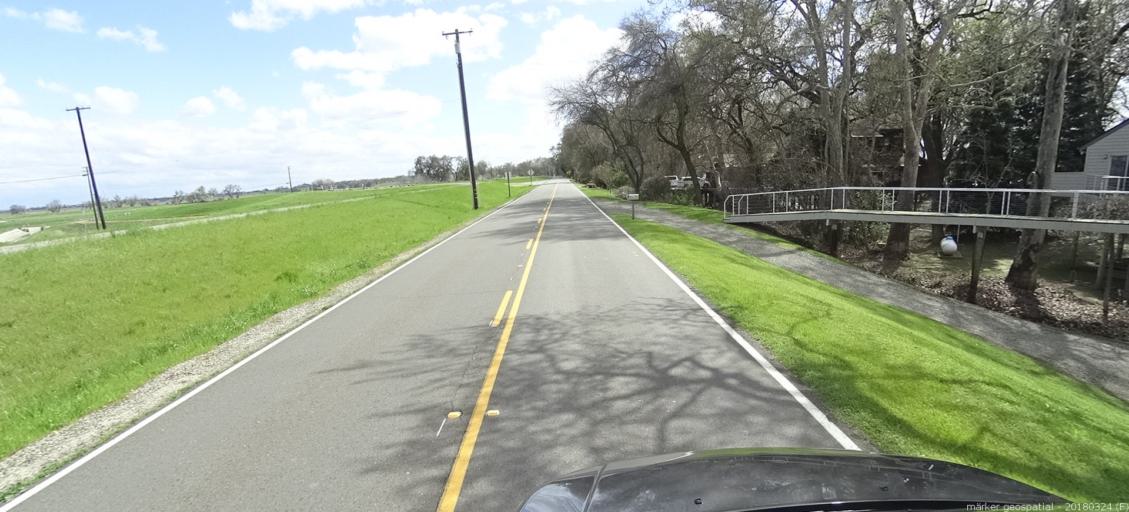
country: US
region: California
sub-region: Yolo County
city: Woodland
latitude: 38.6868
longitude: -121.6323
